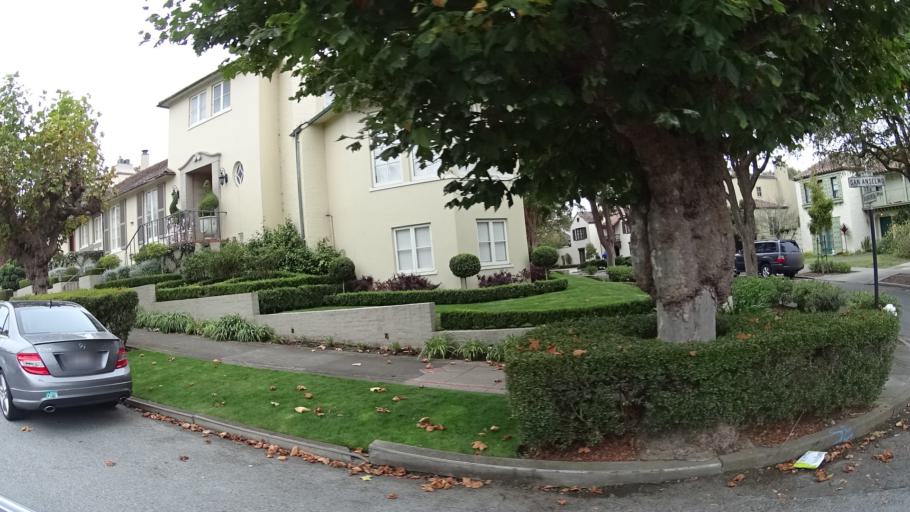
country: US
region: California
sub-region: San Mateo County
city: Daly City
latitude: 37.7363
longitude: -122.4652
